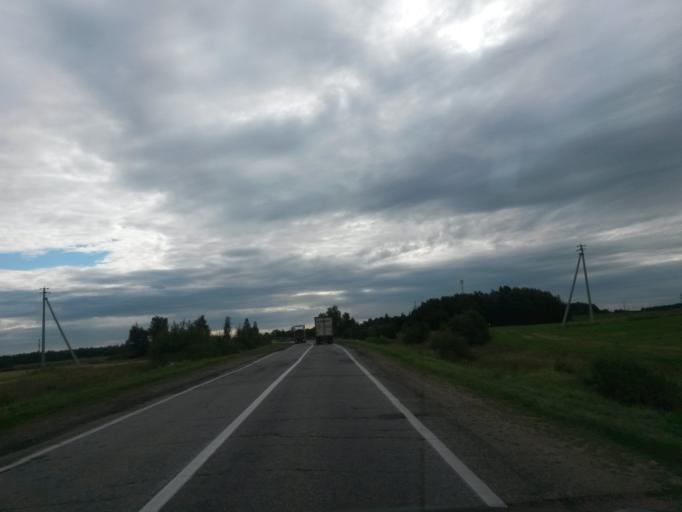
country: RU
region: Jaroslavl
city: Gavrilov-Yam
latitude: 57.3082
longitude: 39.9210
